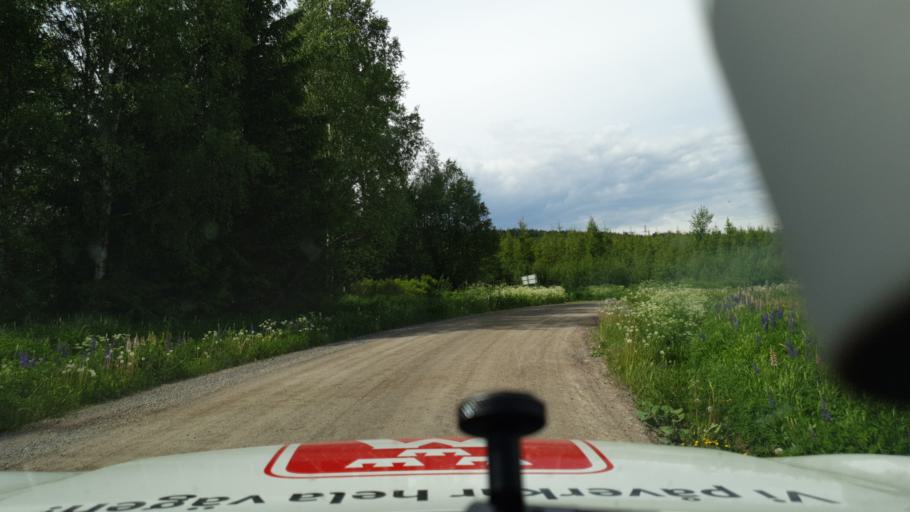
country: SE
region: Vaermland
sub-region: Torsby Kommun
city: Torsby
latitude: 59.9485
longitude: 12.8972
